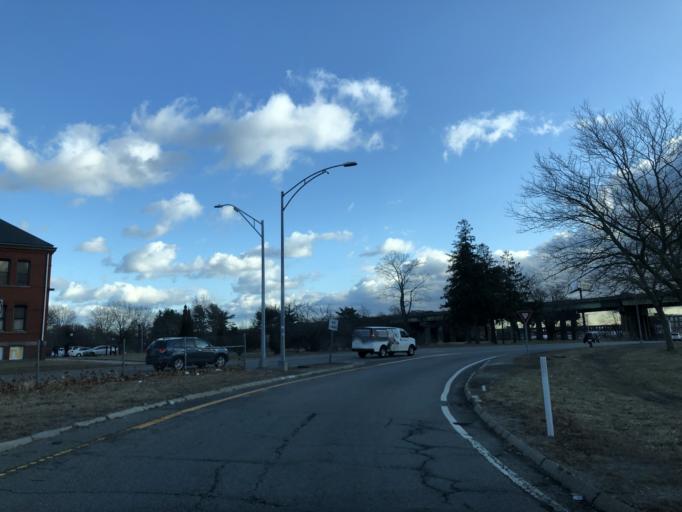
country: US
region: Massachusetts
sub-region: Bristol County
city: New Bedford
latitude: 41.6557
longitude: -70.9293
